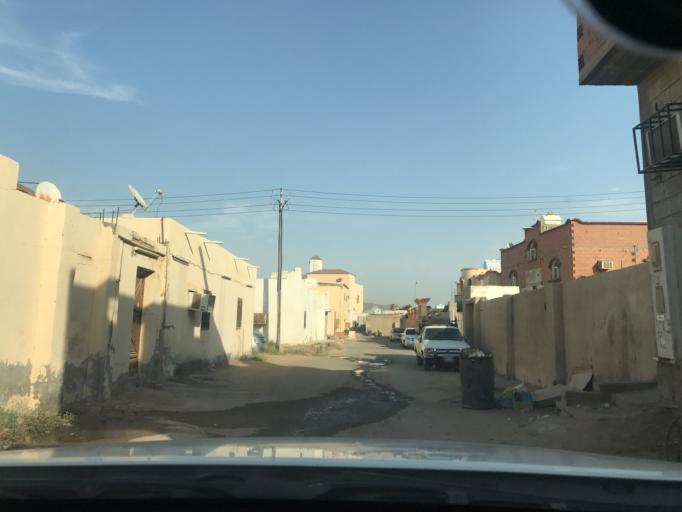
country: SA
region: Makkah
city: Al Jumum
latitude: 21.4398
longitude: 39.5233
